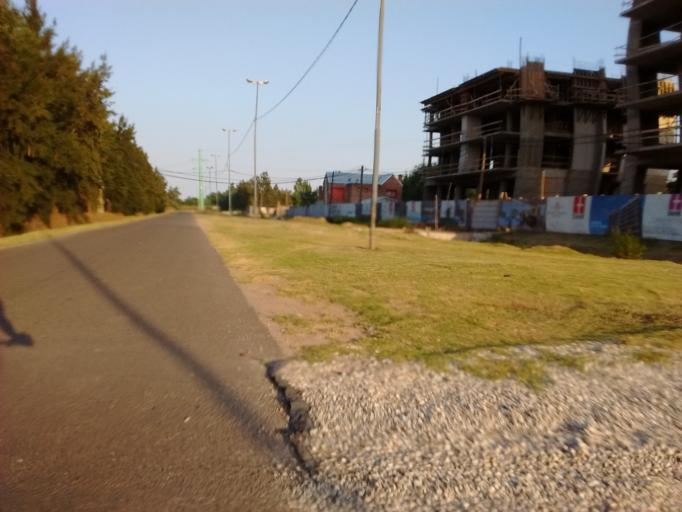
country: AR
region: Santa Fe
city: Funes
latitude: -32.9144
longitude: -60.7544
